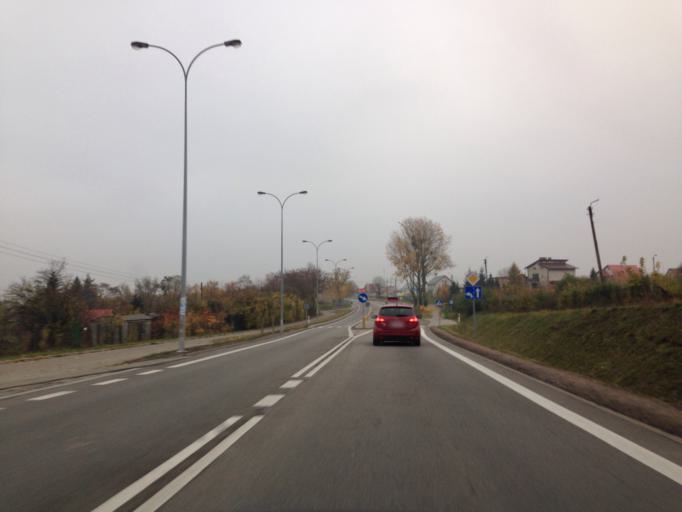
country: PL
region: Pomeranian Voivodeship
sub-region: Powiat gdanski
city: Legowo
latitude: 54.2115
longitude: 18.6579
